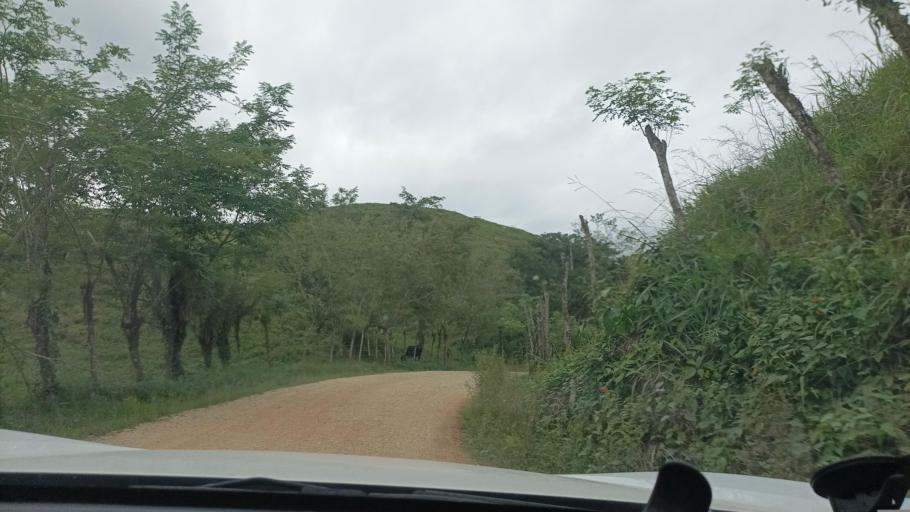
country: MX
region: Veracruz
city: Hidalgotitlan
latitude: 17.6113
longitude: -94.5217
